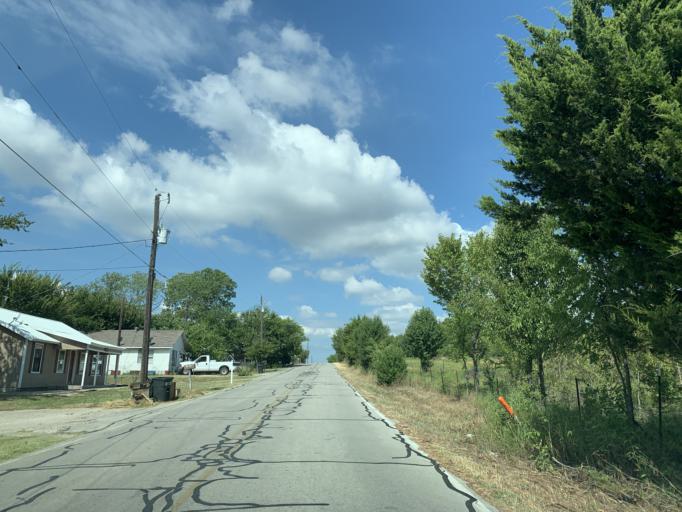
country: US
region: Texas
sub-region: Tarrant County
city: Azle
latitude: 32.8742
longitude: -97.5326
